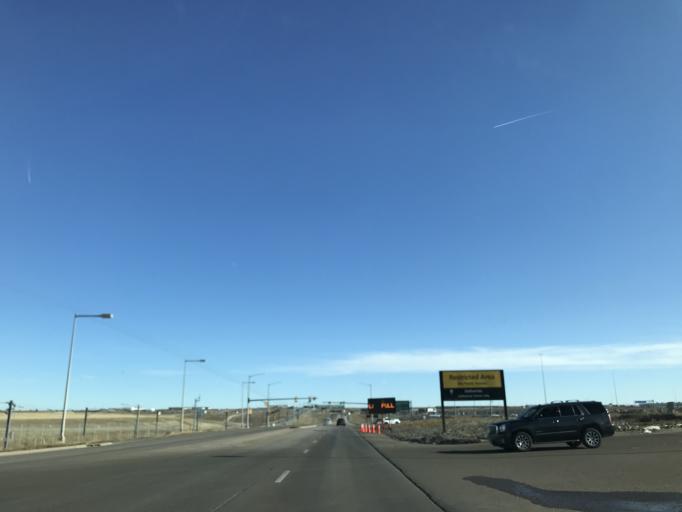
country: US
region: Colorado
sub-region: Weld County
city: Lochbuie
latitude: 39.8379
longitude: -104.6889
